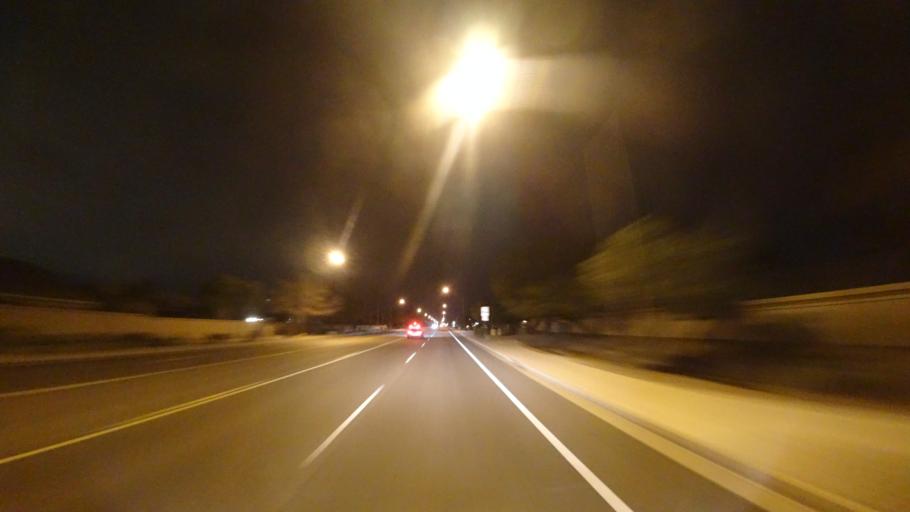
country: US
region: Arizona
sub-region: Maricopa County
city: Gilbert
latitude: 33.3701
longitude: -111.7392
